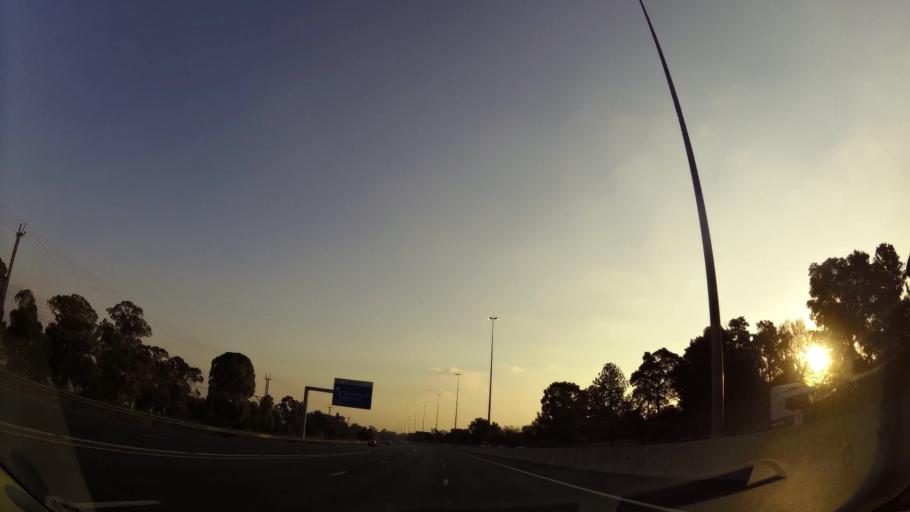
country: ZA
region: Gauteng
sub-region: Ekurhuleni Metropolitan Municipality
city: Benoni
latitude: -26.1775
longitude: 28.3270
